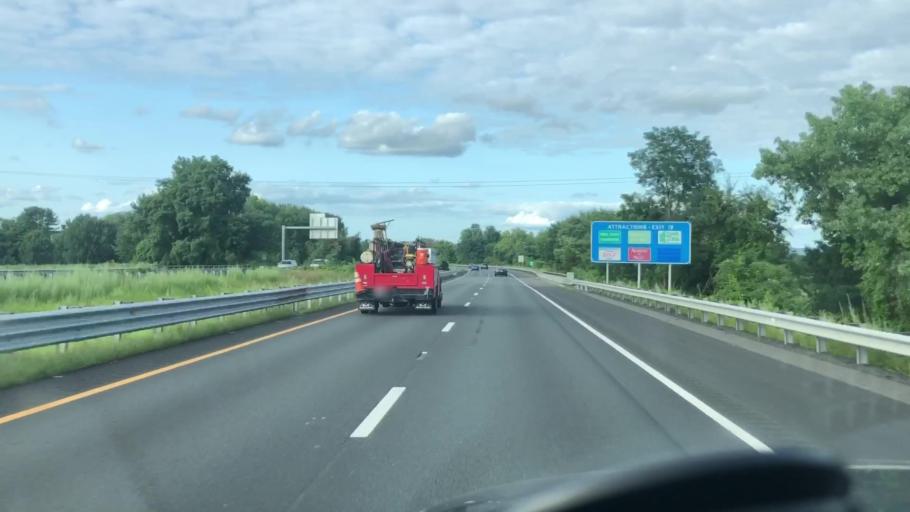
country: US
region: Massachusetts
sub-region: Hampshire County
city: Northampton
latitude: 42.3109
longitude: -72.6196
